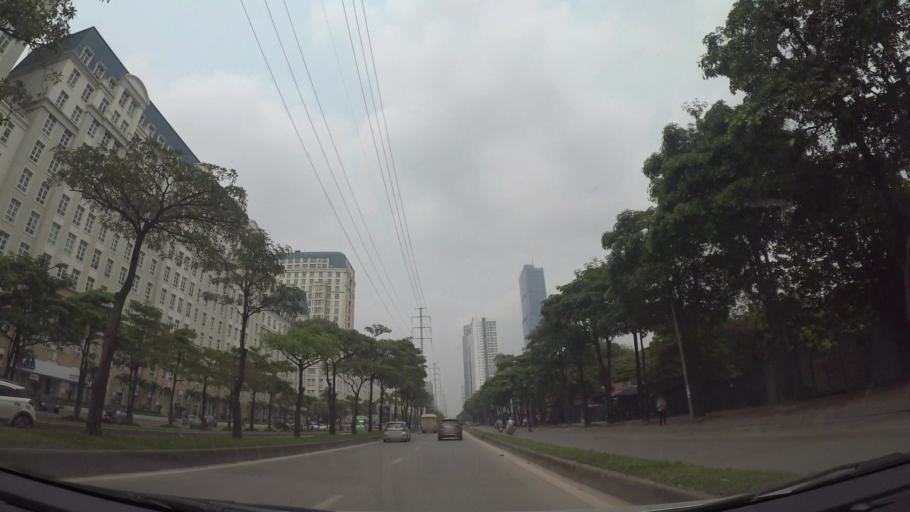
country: VN
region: Ha Noi
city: Cau Dien
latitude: 21.0132
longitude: 105.7760
